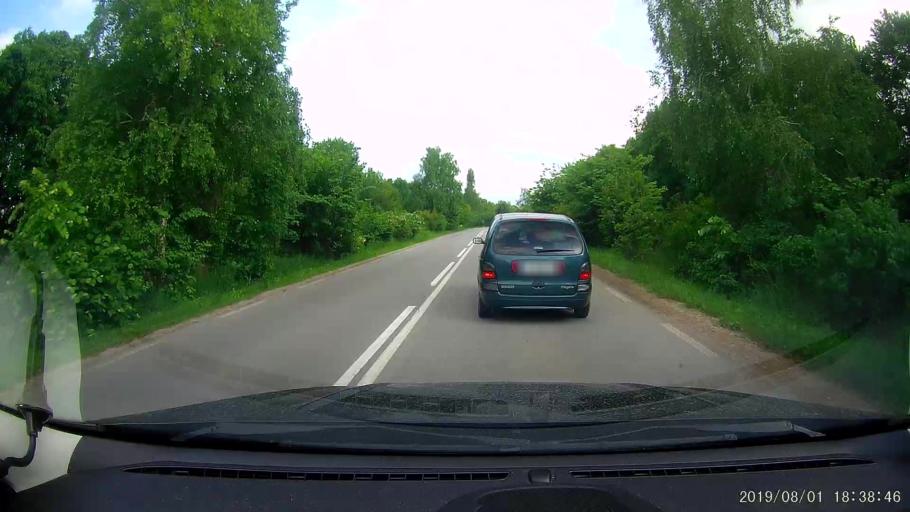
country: BG
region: Shumen
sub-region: Obshtina Khitrino
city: Gara Khitrino
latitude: 43.3977
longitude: 26.9166
